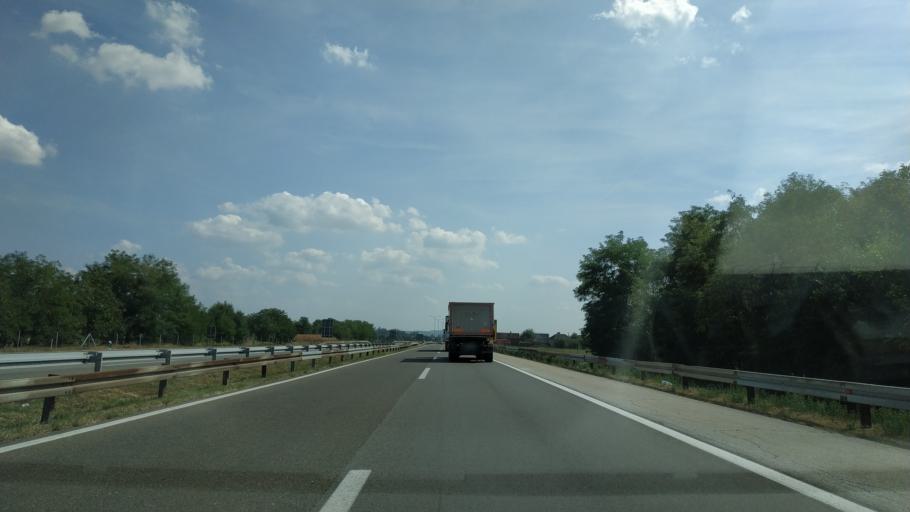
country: RS
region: Central Serbia
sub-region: Sumadijski Okrug
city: Lapovo
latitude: 44.2475
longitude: 21.1146
